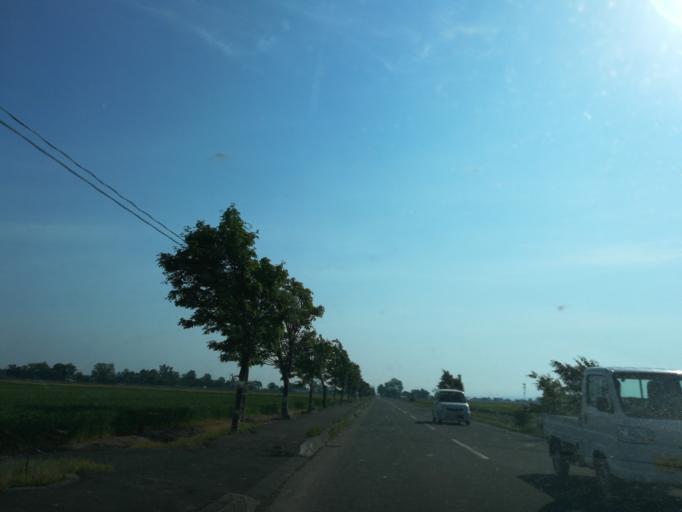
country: JP
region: Hokkaido
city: Iwamizawa
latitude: 43.1508
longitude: 141.6667
